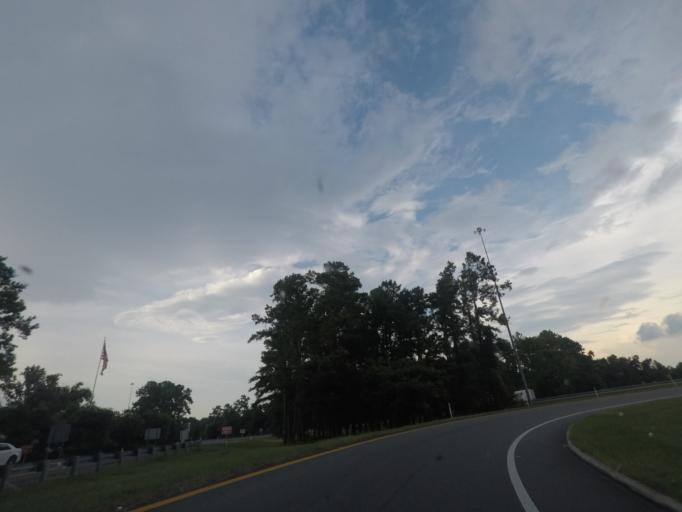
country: US
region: Florida
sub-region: Alachua County
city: Gainesville
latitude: 29.6024
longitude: -82.3749
